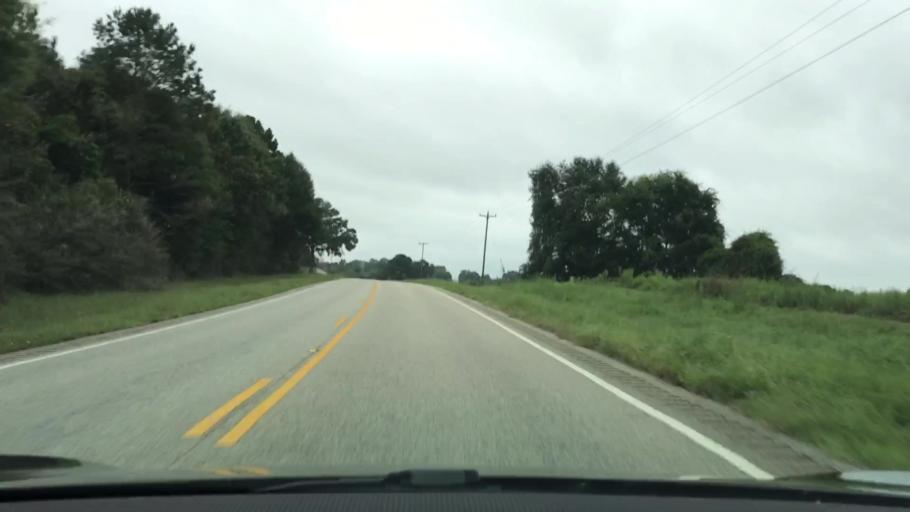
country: US
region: Alabama
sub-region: Coffee County
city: Elba
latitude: 31.3577
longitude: -86.1199
